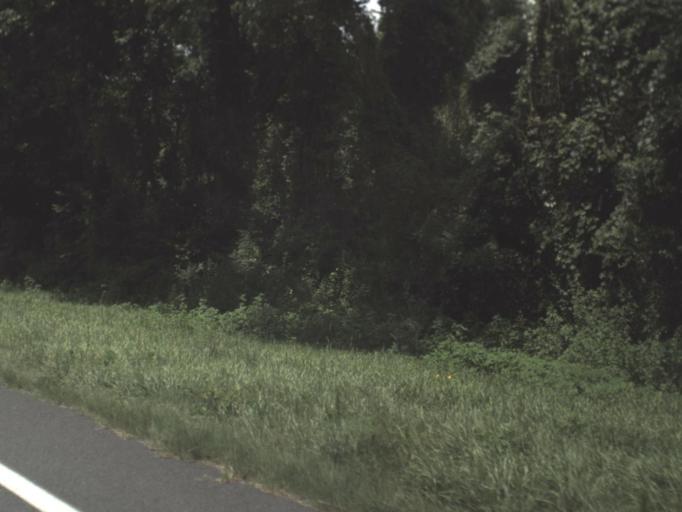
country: US
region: Florida
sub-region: Suwannee County
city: Wellborn
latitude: 30.3668
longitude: -82.7949
